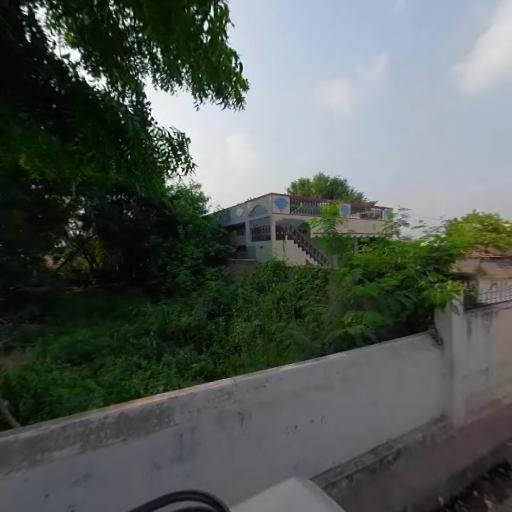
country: IN
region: Telangana
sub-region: Nalgonda
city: Suriapet
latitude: 17.1675
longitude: 79.5105
